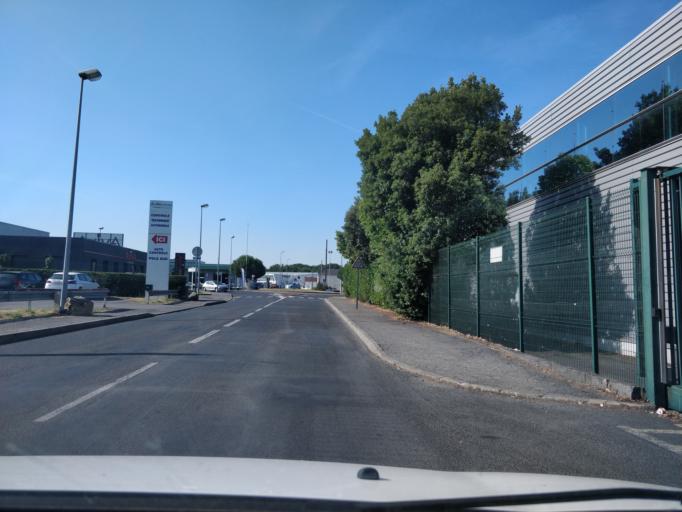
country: FR
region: Pays de la Loire
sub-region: Departement de la Loire-Atlantique
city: Vertou
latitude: 47.1879
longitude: -1.4640
